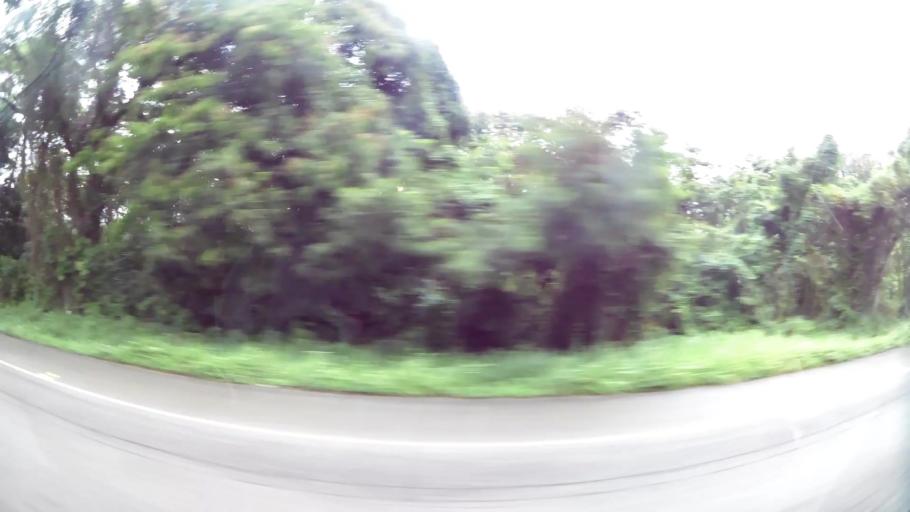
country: DO
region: San Cristobal
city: Villa Altagracia
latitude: 18.6333
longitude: -70.1677
